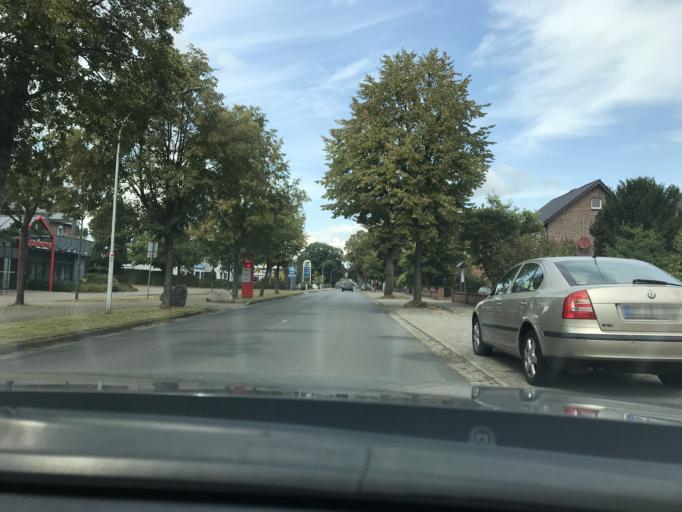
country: DE
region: Lower Saxony
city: Suderburg
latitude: 52.9014
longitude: 10.4381
